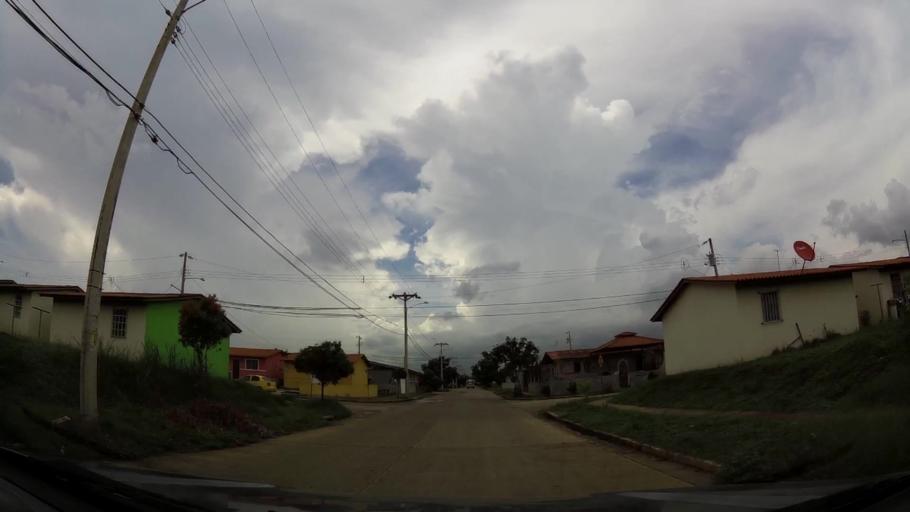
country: PA
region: Panama
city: Cabra Numero Uno
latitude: 9.1173
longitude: -79.3213
